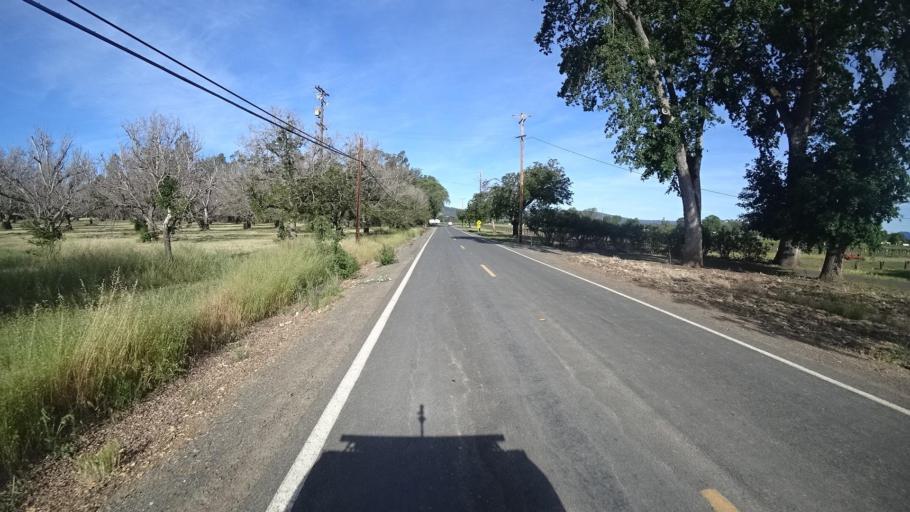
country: US
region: California
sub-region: Lake County
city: Kelseyville
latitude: 39.0038
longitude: -122.8824
